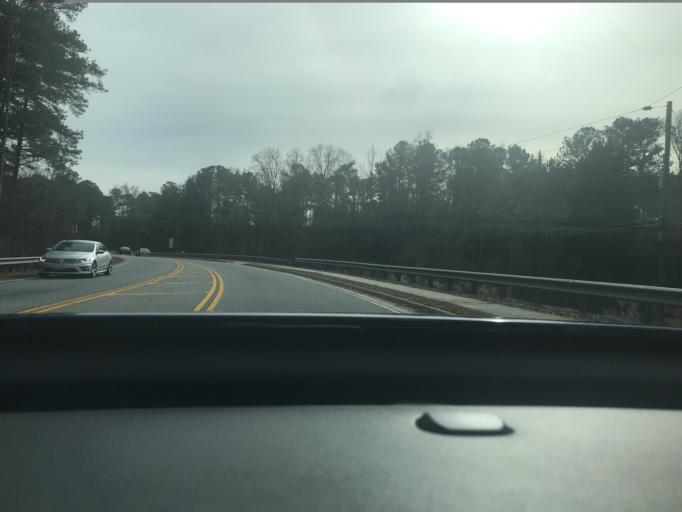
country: US
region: Georgia
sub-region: Gwinnett County
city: Mountain Park
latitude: 33.8746
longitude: -84.0913
